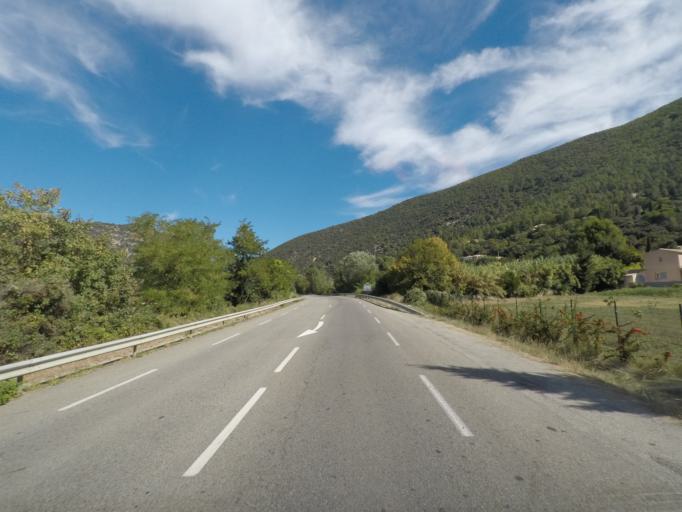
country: FR
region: Rhone-Alpes
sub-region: Departement de la Drome
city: Nyons
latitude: 44.3602
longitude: 5.1483
